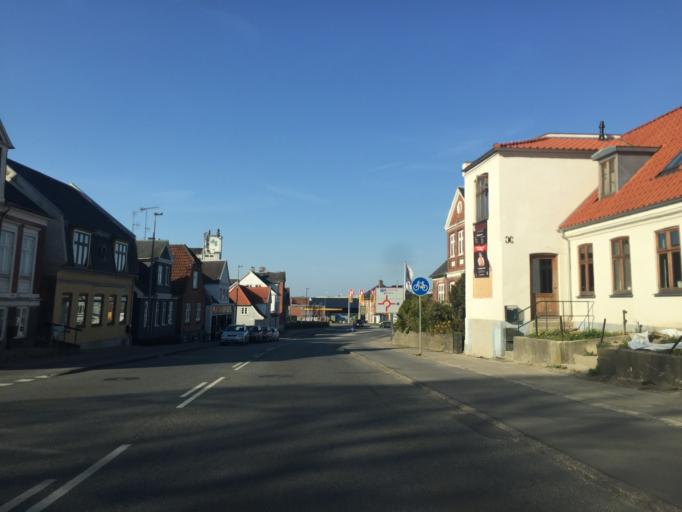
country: DK
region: South Denmark
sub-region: Svendborg Kommune
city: Svendborg
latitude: 55.0643
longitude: 10.6217
